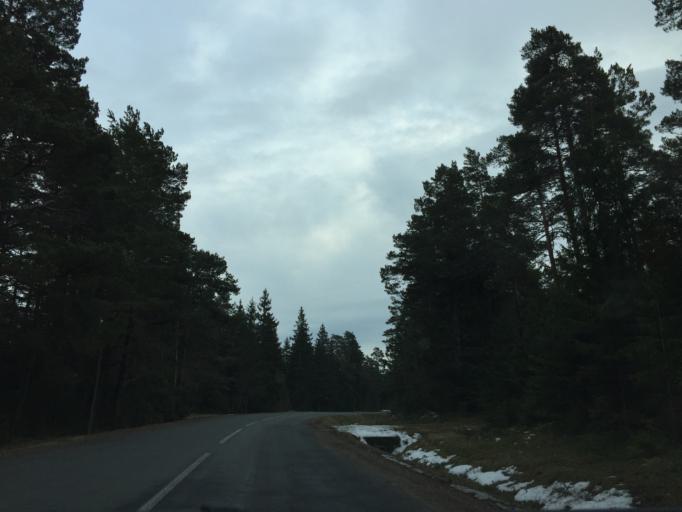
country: EE
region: Saare
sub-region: Kuressaare linn
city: Kuressaare
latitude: 58.4343
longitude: 22.0666
